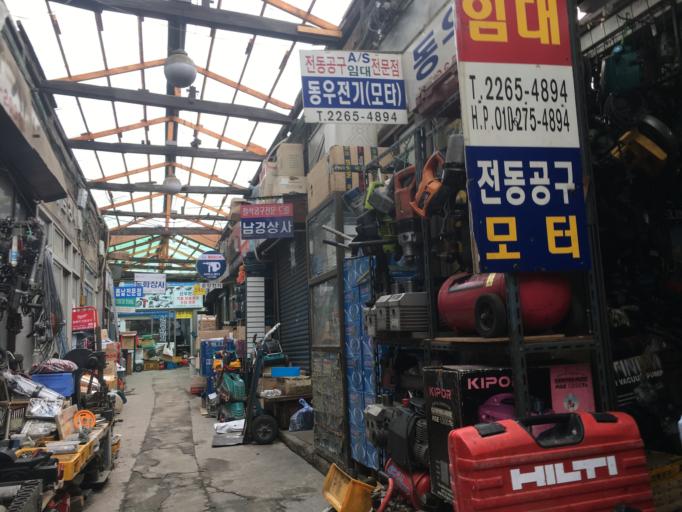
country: KR
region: Seoul
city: Seoul
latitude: 37.5687
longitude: 126.9932
